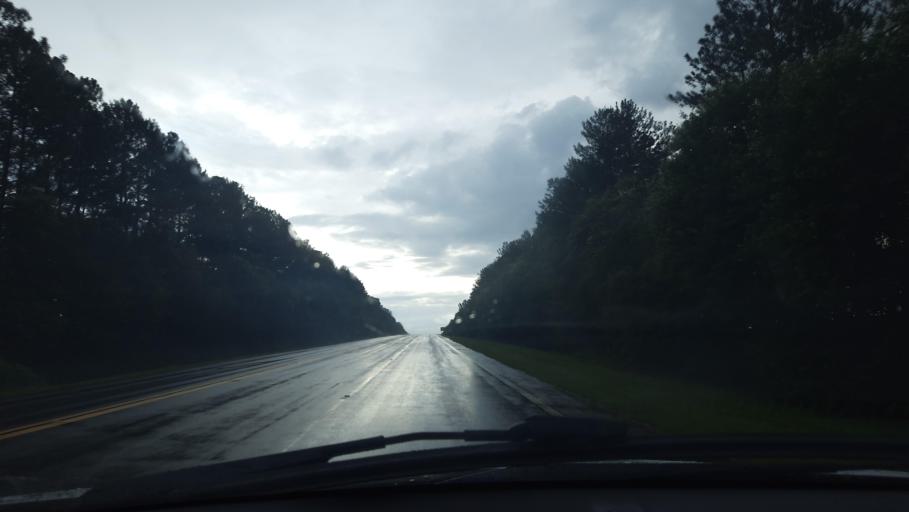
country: BR
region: Sao Paulo
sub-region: Casa Branca
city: Casa Branca
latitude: -21.7627
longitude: -47.0241
